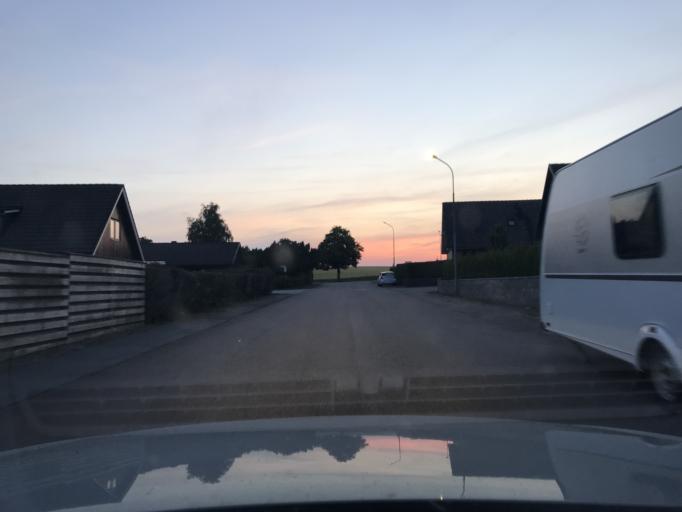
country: SE
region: Skane
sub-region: Svalovs Kommun
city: Svaloev
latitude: 55.9148
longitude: 13.0963
